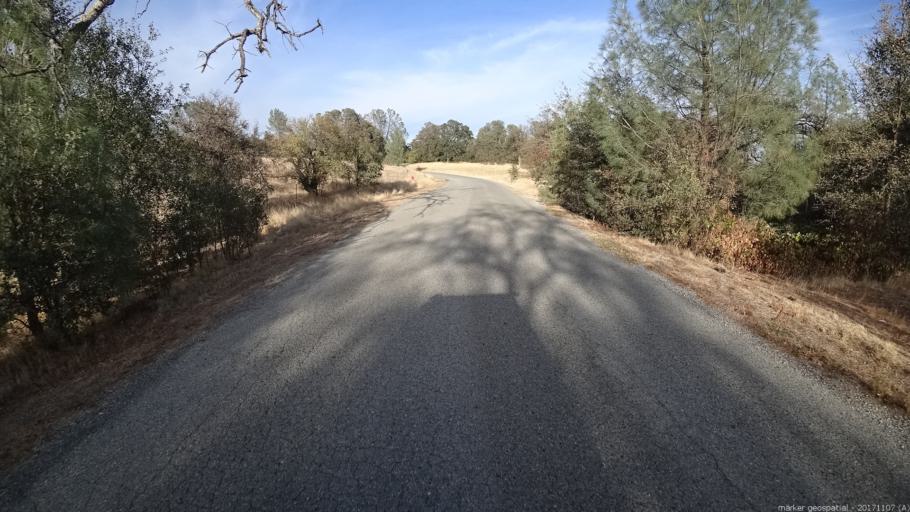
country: US
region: California
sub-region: Shasta County
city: Shasta
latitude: 40.5157
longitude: -122.4708
